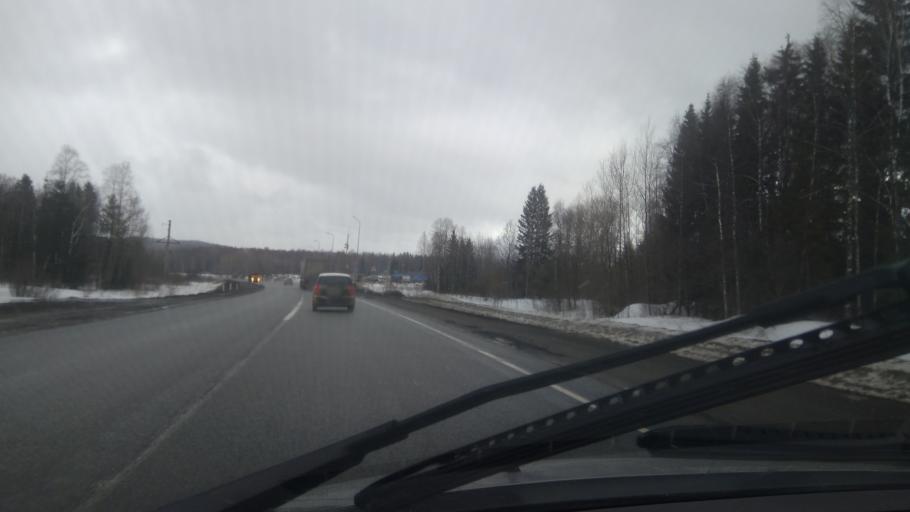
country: RU
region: Sverdlovsk
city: Ufimskiy
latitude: 56.7831
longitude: 58.3970
